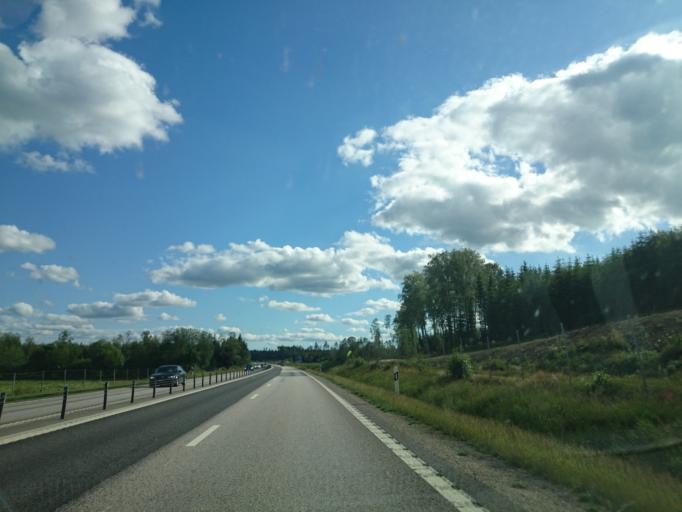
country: SE
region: Kronoberg
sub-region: Ljungby Kommun
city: Ljungby
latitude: 56.7986
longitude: 13.8931
